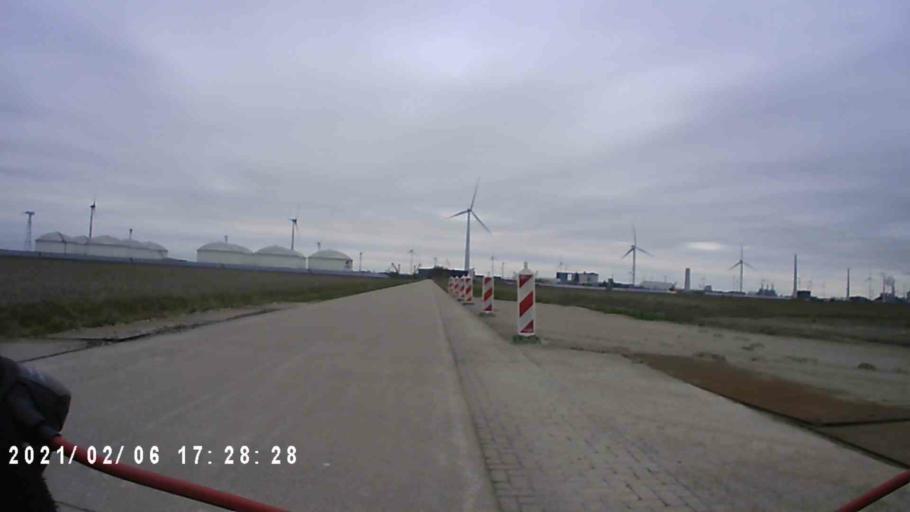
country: NL
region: Groningen
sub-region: Gemeente Appingedam
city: Appingedam
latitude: 53.4414
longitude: 6.8005
